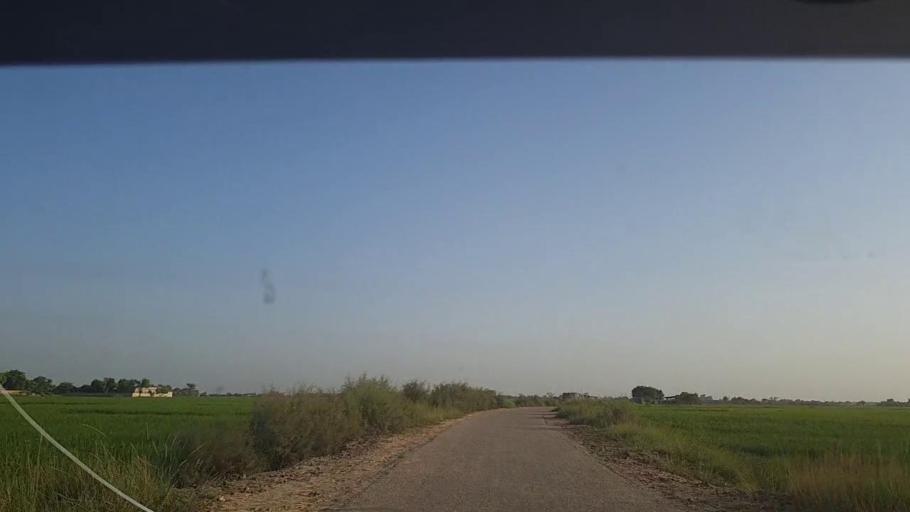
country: PK
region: Sindh
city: Thul
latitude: 28.1984
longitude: 68.8740
